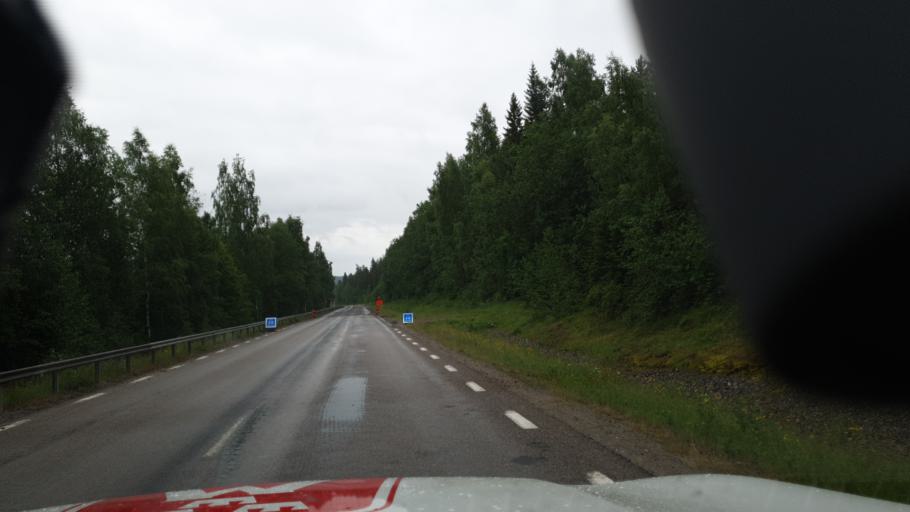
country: SE
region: Vaesterbotten
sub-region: Vannas Kommun
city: Vaennaes
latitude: 63.7881
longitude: 19.8276
